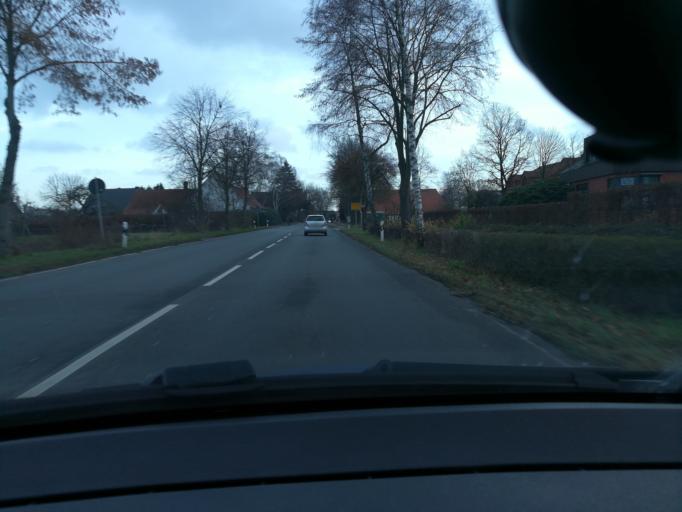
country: DE
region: North Rhine-Westphalia
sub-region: Regierungsbezirk Detmold
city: Hille
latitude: 52.3216
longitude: 8.7879
